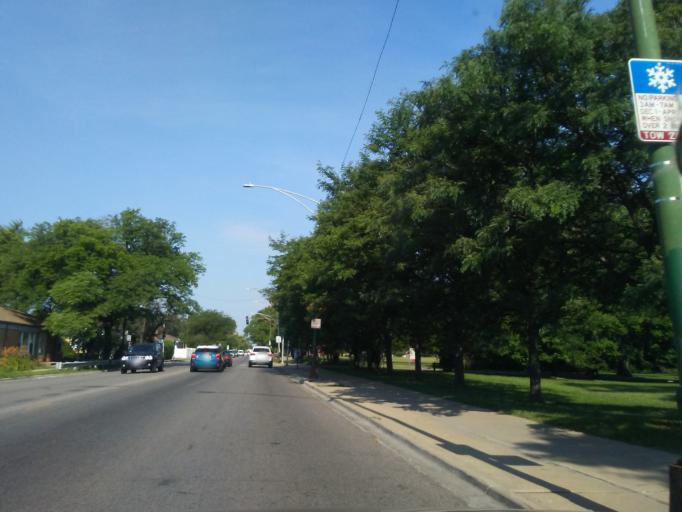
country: US
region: Illinois
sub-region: Cook County
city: Lincolnwood
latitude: 41.9755
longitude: -87.7373
